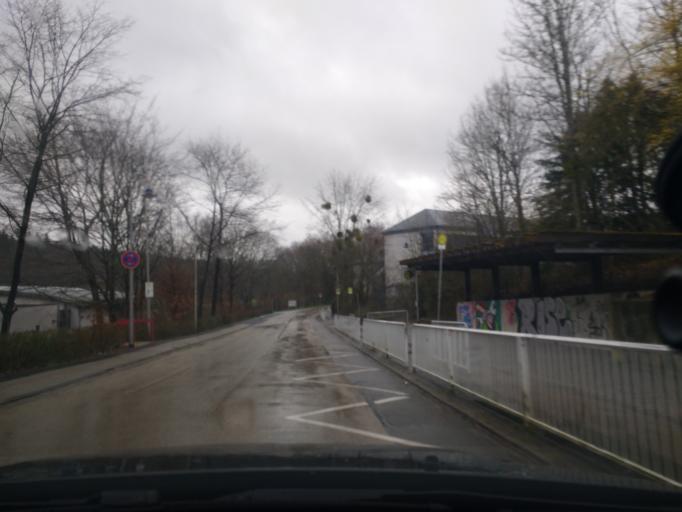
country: DE
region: Rheinland-Pfalz
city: Konz
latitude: 49.6930
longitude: 6.5850
